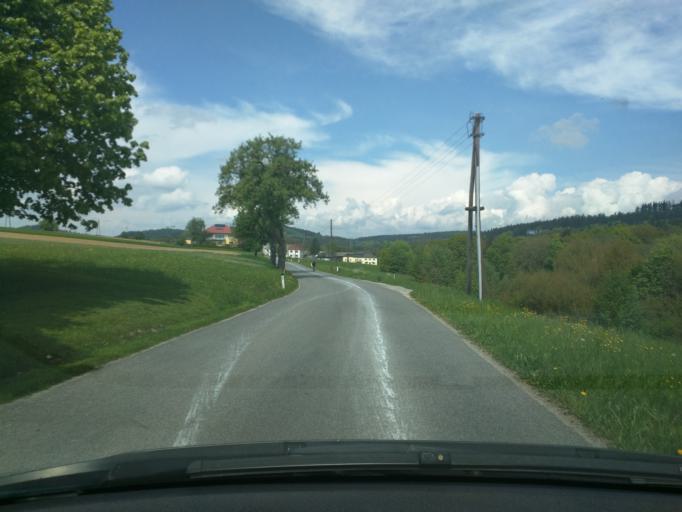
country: AT
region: Lower Austria
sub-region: Politischer Bezirk Melk
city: Blindenmarkt
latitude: 48.1359
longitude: 14.9937
